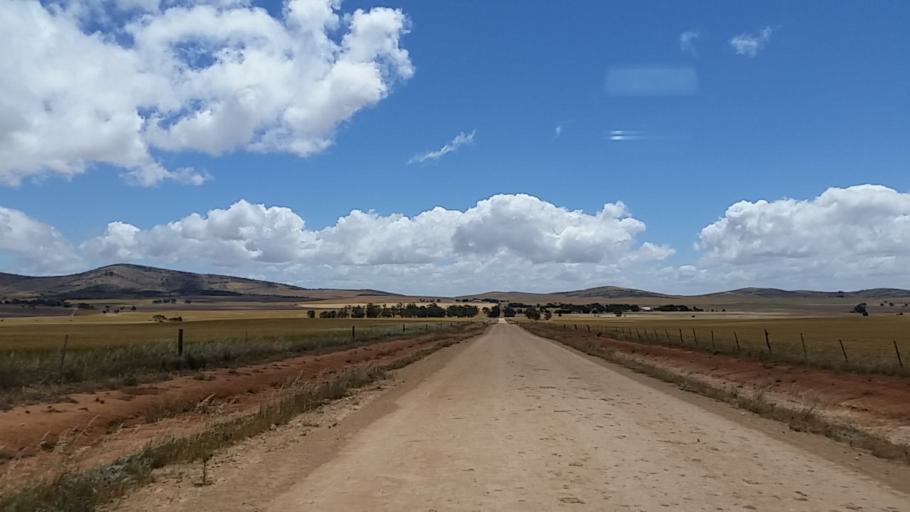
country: AU
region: South Australia
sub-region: Peterborough
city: Peterborough
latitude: -32.8539
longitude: 138.5583
